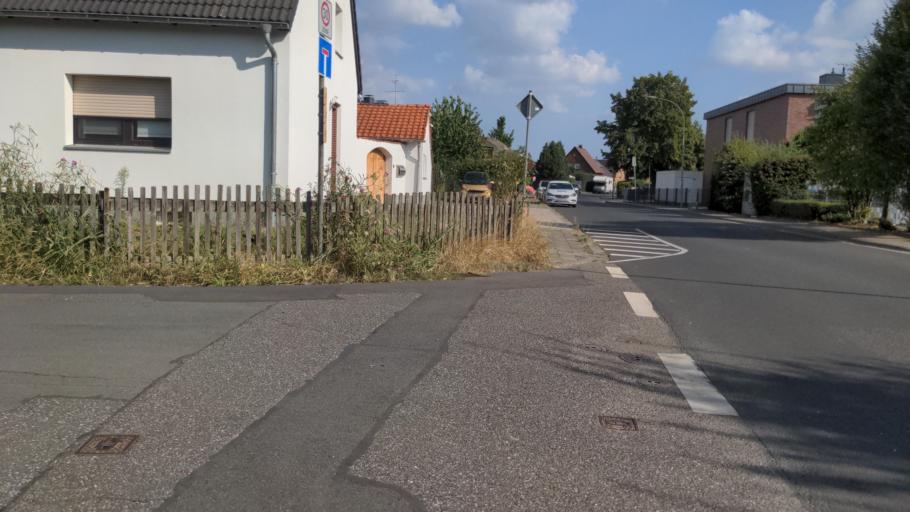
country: DE
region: North Rhine-Westphalia
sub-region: Regierungsbezirk Dusseldorf
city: Kaarst
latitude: 51.2171
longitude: 6.5734
